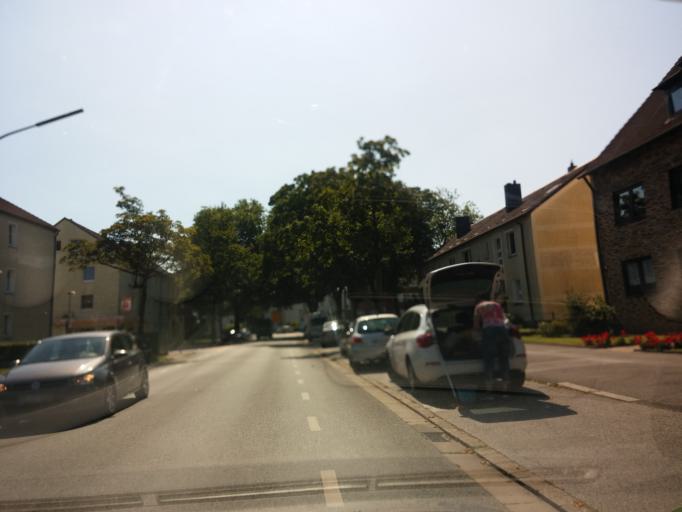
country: DE
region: North Rhine-Westphalia
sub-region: Regierungsbezirk Munster
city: Gelsenkirchen
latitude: 51.5441
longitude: 7.0640
